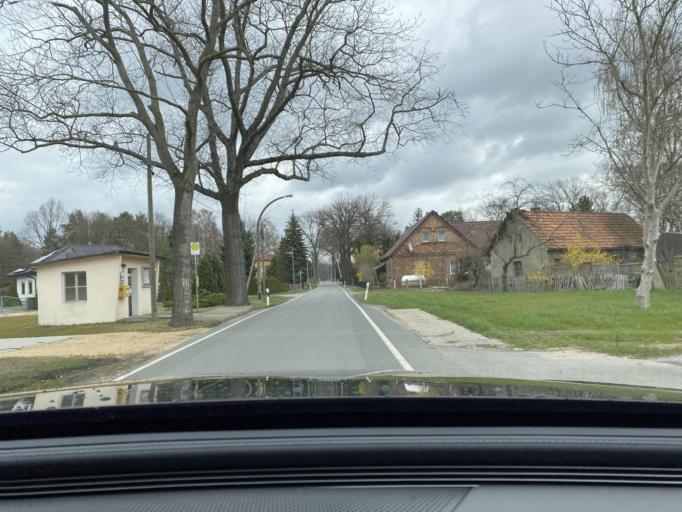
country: DE
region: Saxony
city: Uhyst
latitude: 51.3355
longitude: 14.4881
